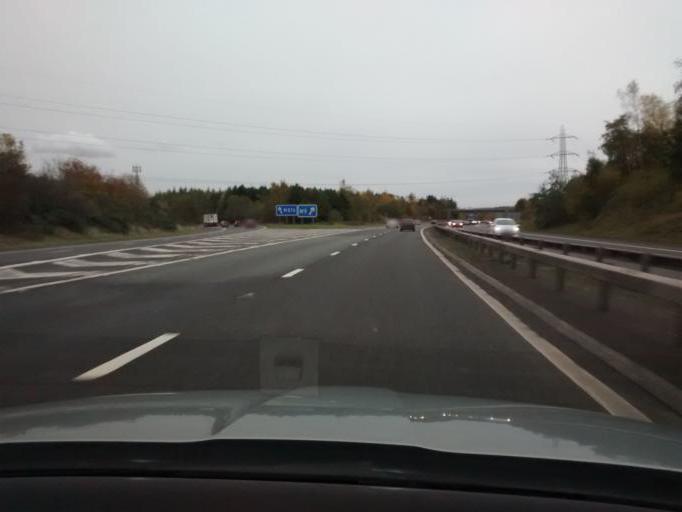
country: GB
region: Scotland
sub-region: Falkirk
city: Airth
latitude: 56.0447
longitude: -3.7890
